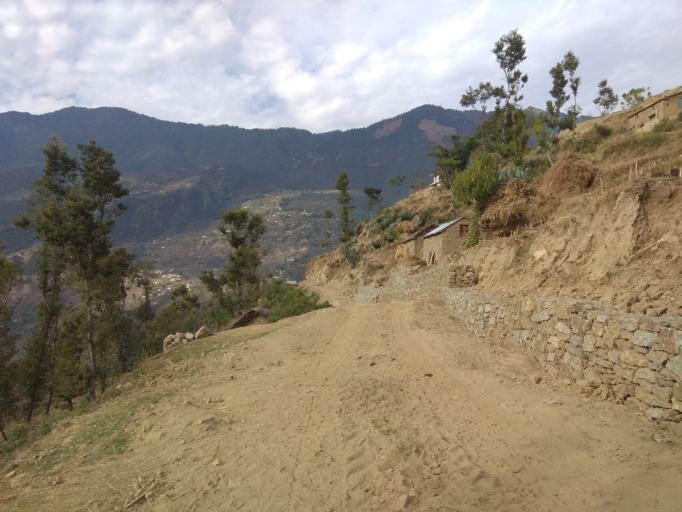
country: NP
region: Far Western
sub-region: Seti Zone
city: Achham
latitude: 29.2451
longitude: 81.6271
